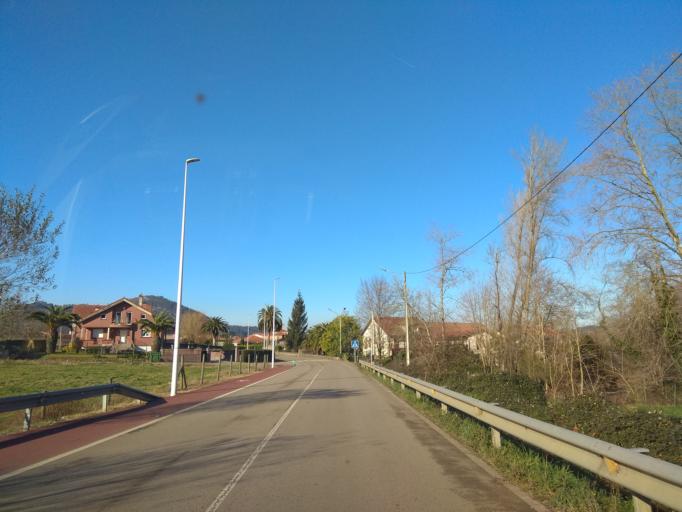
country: ES
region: Cantabria
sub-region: Provincia de Cantabria
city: Entrambasaguas
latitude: 43.3747
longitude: -3.6737
